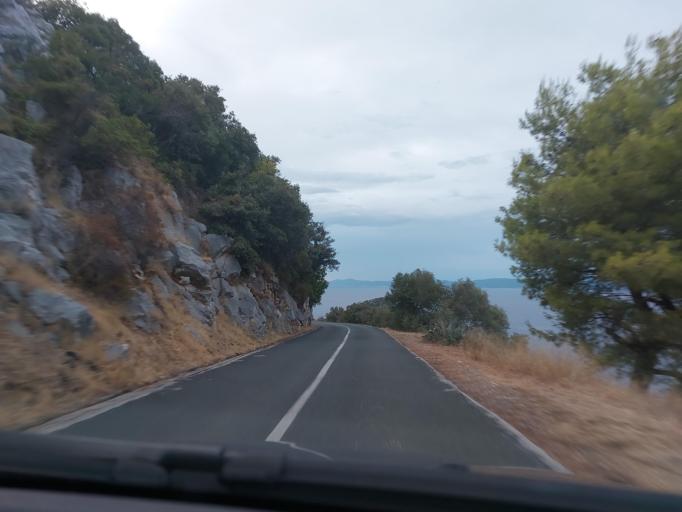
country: HR
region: Dubrovacko-Neretvanska
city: Smokvica
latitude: 42.7686
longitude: 16.8857
